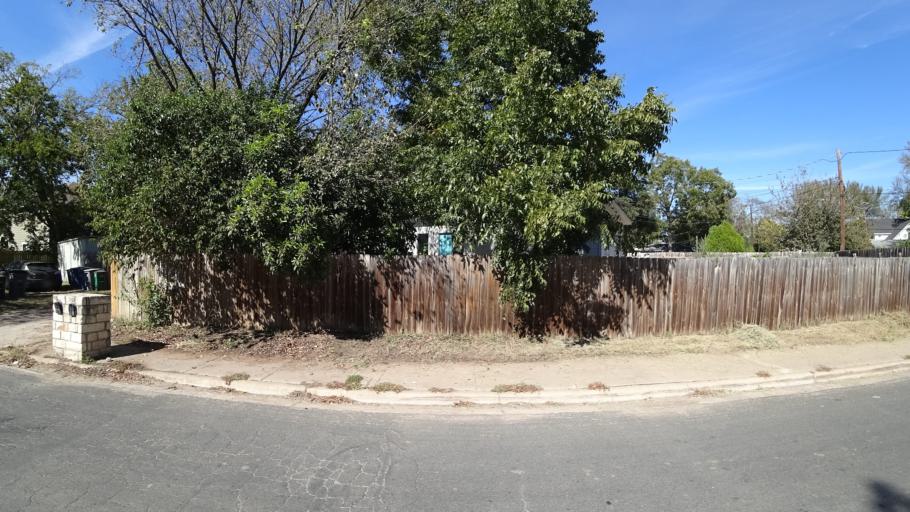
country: US
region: Texas
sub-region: Travis County
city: Austin
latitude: 30.2675
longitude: -97.6854
